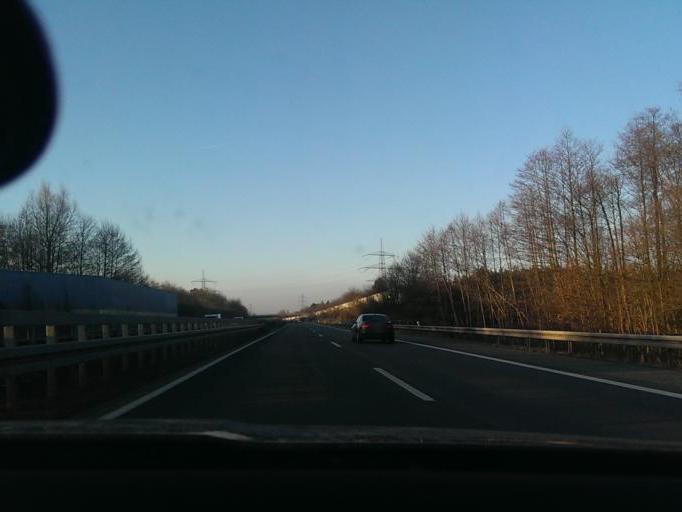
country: DE
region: North Rhine-Westphalia
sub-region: Regierungsbezirk Detmold
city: Oerlinghausen
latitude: 51.8891
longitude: 8.6419
